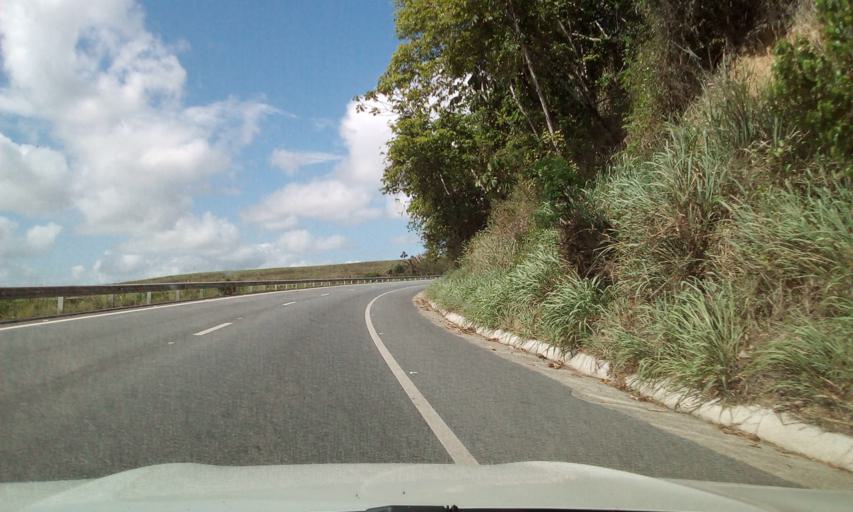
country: BR
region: Alagoas
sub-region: Rio Largo
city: Rio Largo
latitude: -9.4610
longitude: -35.8801
